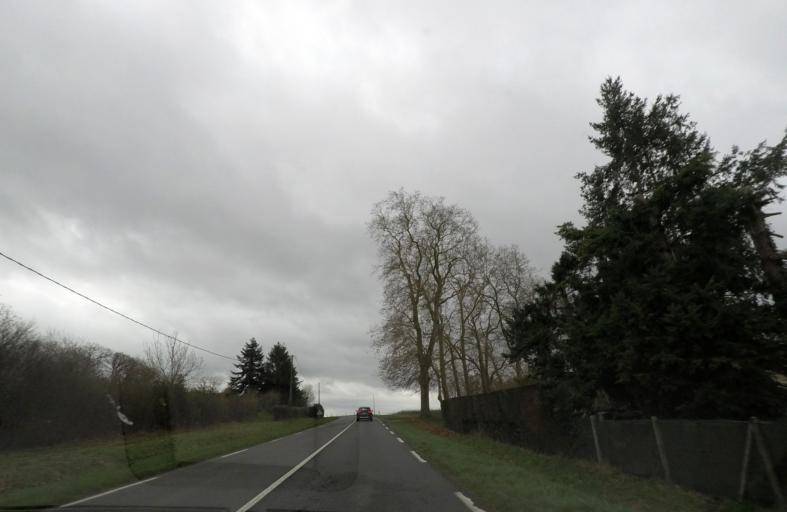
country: FR
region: Centre
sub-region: Departement du Loir-et-Cher
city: Cour-Cheverny
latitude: 47.5233
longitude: 1.4337
